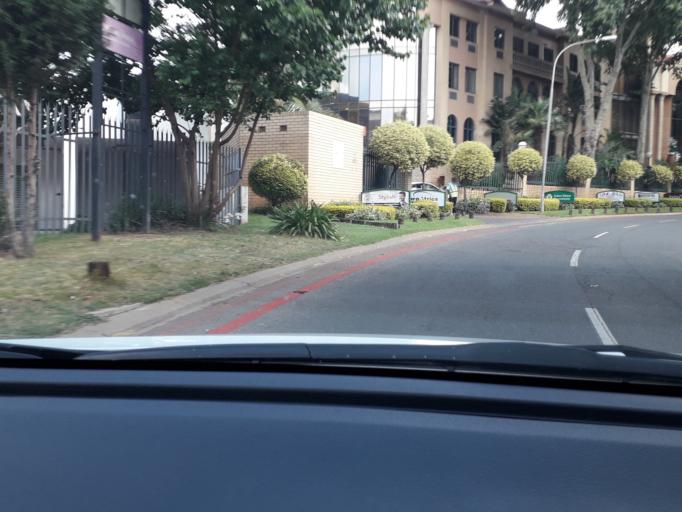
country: ZA
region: Gauteng
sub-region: City of Johannesburg Metropolitan Municipality
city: Johannesburg
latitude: -26.1813
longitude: 28.1084
